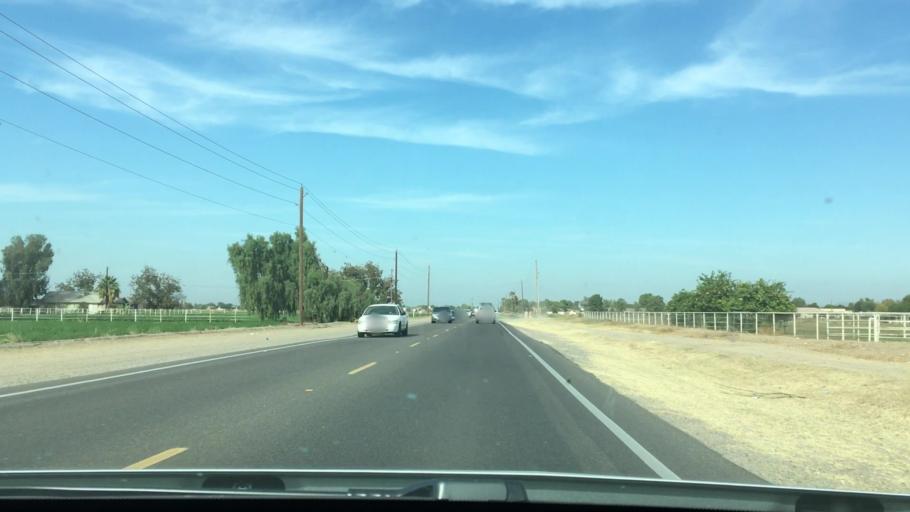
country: US
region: Arizona
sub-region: Maricopa County
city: Chandler
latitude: 33.2434
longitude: -111.7554
